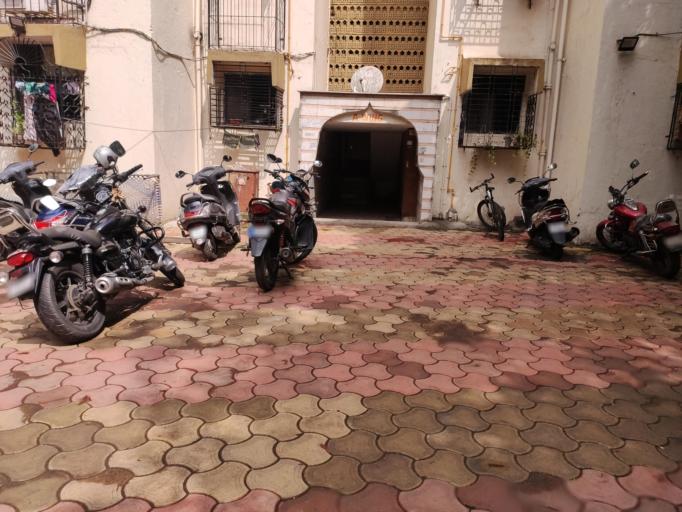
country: IN
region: Maharashtra
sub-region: Mumbai Suburban
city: Borivli
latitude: 19.2506
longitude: 72.8628
